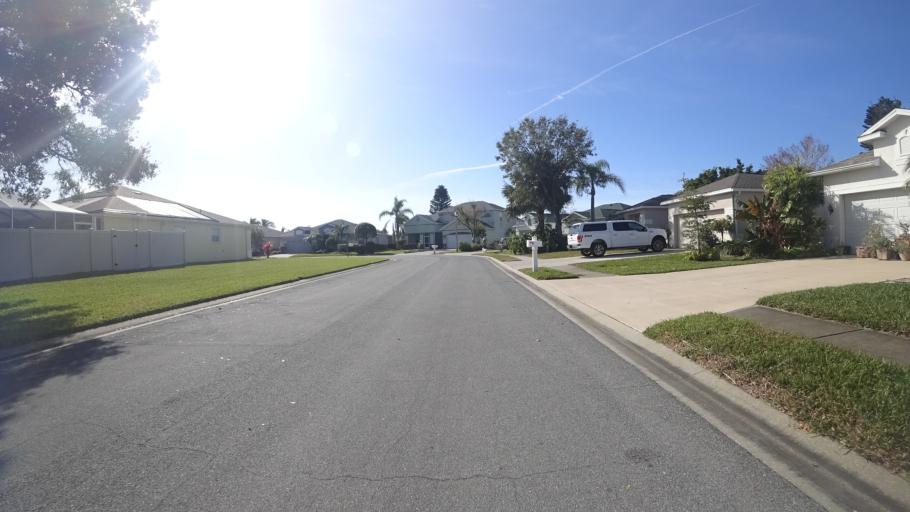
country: US
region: Florida
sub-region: Manatee County
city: South Bradenton
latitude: 27.4536
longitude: -82.6065
